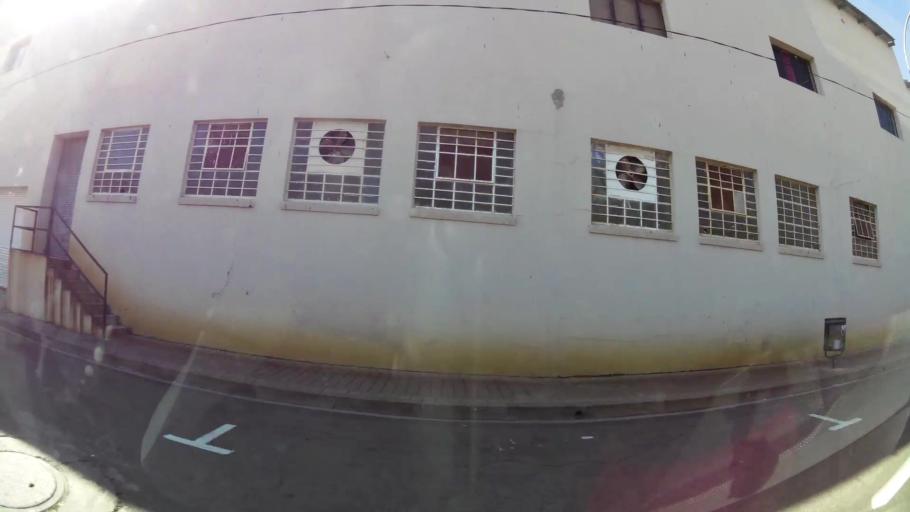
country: ZA
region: Gauteng
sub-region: City of Johannesburg Metropolitan Municipality
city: Johannesburg
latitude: -26.2007
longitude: 28.0608
